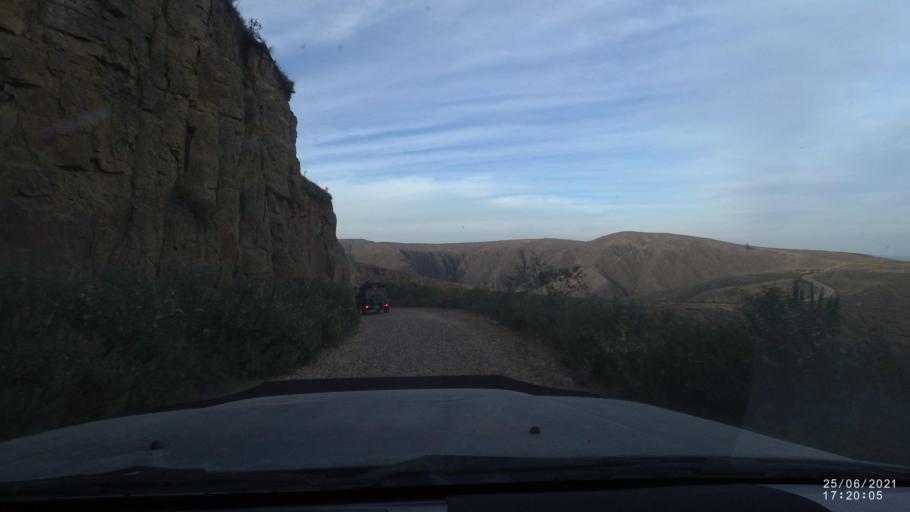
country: BO
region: Cochabamba
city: Arani
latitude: -17.9029
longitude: -65.6909
